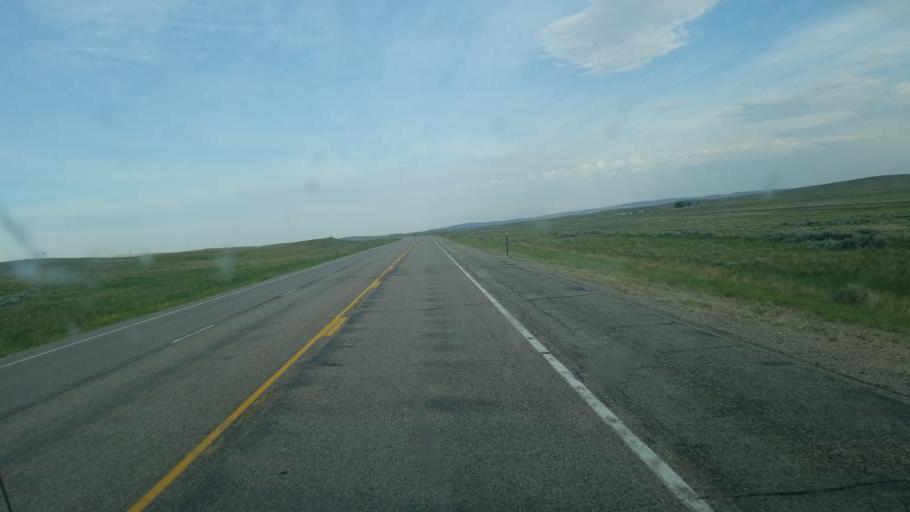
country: US
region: Wyoming
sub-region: Natrona County
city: Mills
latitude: 43.0336
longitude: -106.8883
